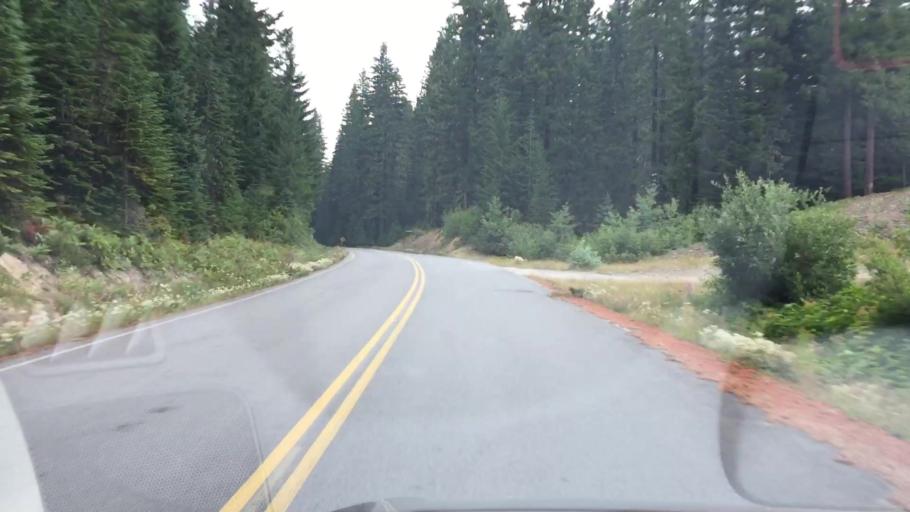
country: US
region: Washington
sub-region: Klickitat County
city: White Salmon
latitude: 46.1591
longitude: -121.6312
